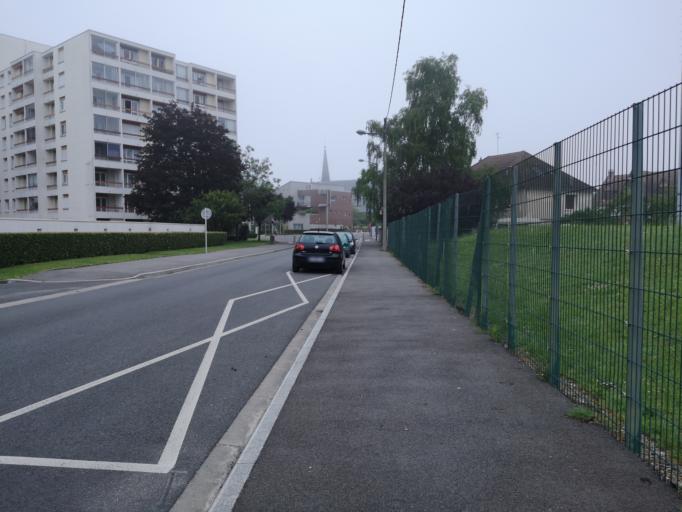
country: FR
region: Centre
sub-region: Departement du Loiret
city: Fleury-les-Aubrais
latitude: 47.9304
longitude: 1.9222
